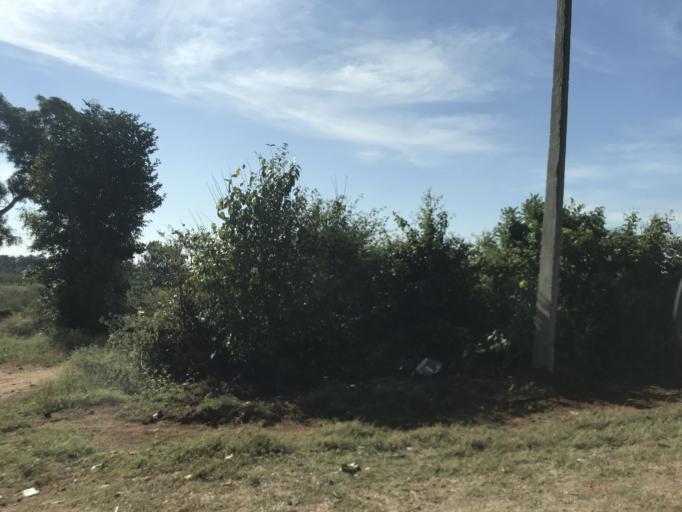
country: IN
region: Karnataka
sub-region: Mysore
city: Mysore
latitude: 12.1981
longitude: 76.5484
